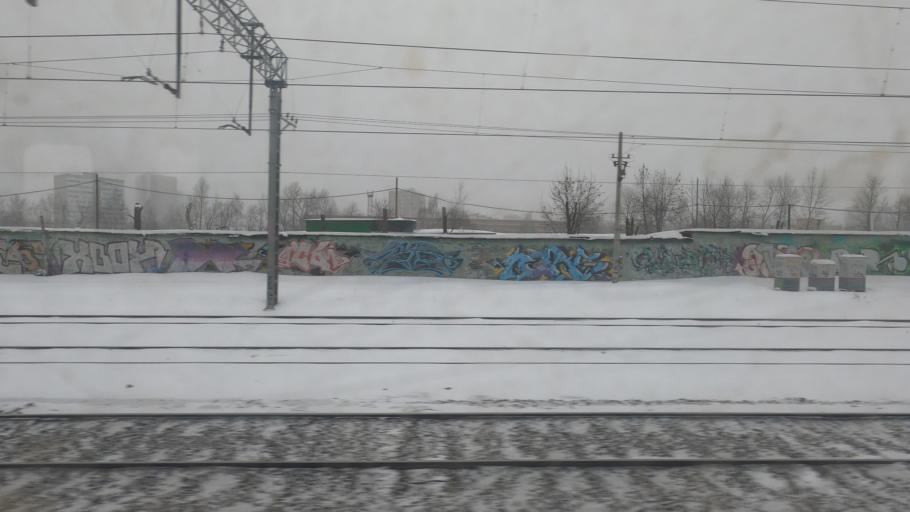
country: RU
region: Moskovskaya
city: Kuskovo
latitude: 55.7469
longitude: 37.8367
